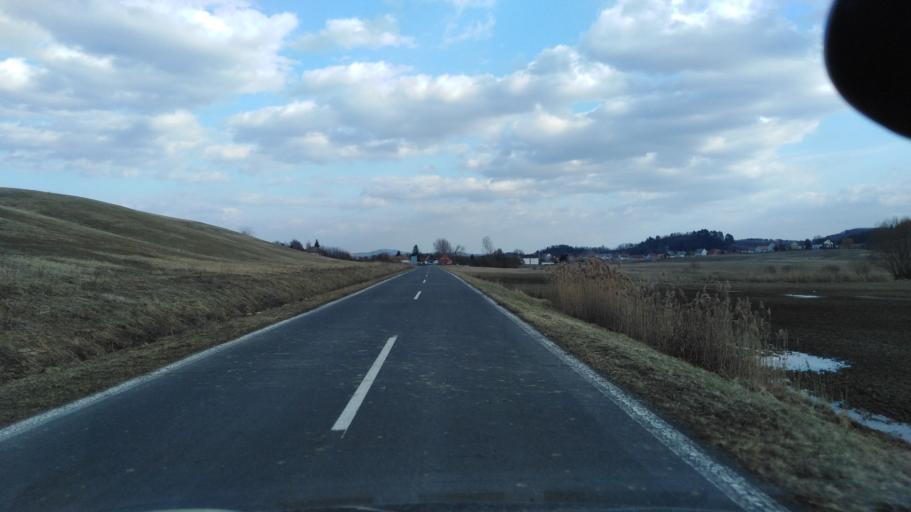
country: HU
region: Nograd
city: Matraterenye
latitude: 48.1521
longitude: 19.9455
